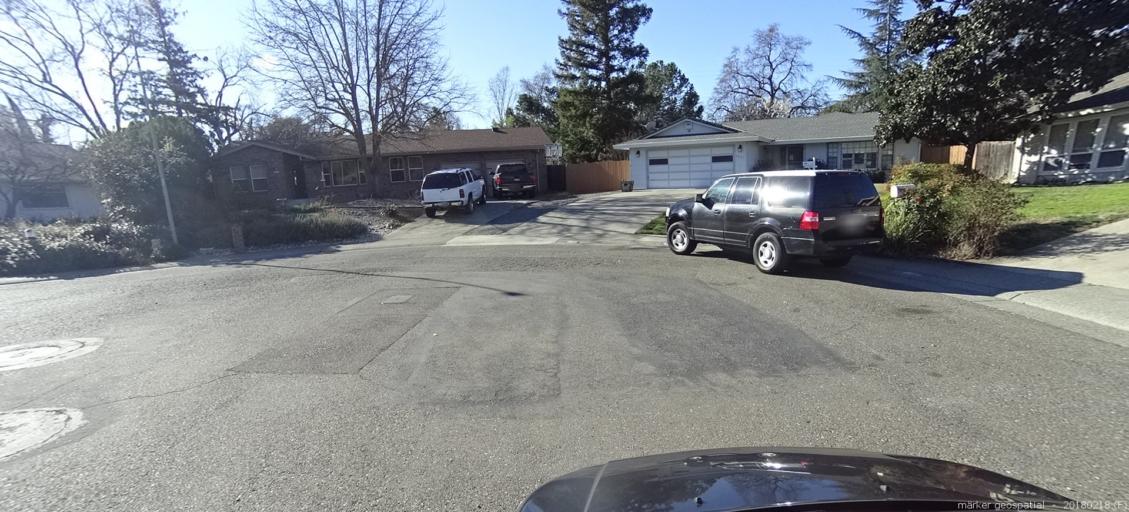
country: US
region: California
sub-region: Sacramento County
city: Orangevale
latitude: 38.6726
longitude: -121.2385
